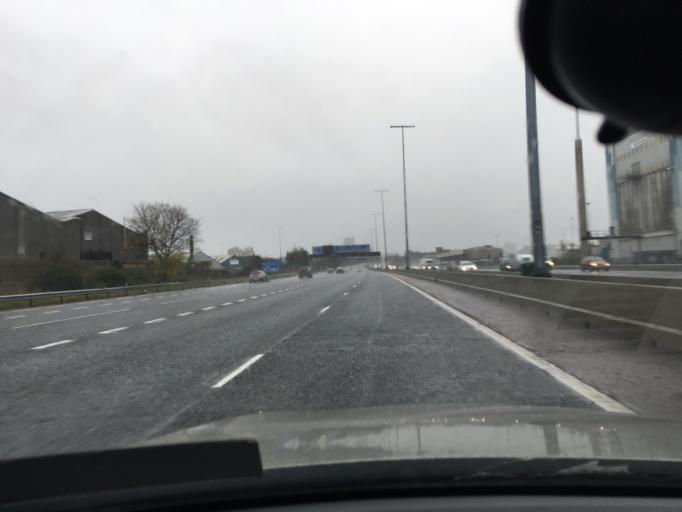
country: GB
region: Northern Ireland
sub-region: City of Belfast
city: Belfast
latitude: 54.6164
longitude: -5.9208
